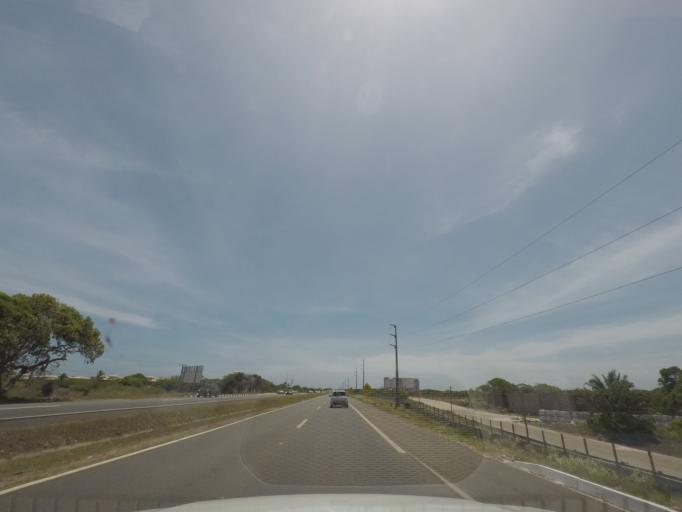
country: BR
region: Bahia
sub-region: Camacari
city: Camacari
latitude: -12.6612
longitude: -38.0912
